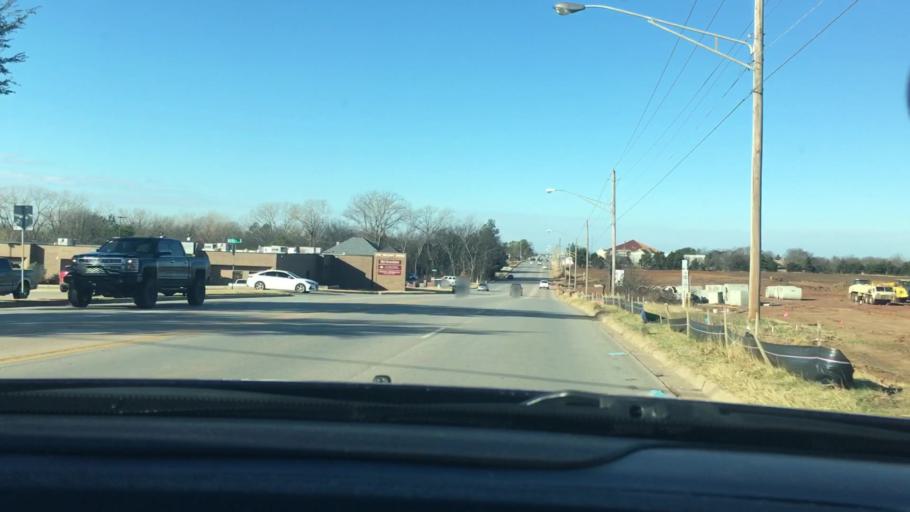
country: US
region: Oklahoma
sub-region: Carter County
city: Ardmore
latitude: 34.1876
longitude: -97.1474
